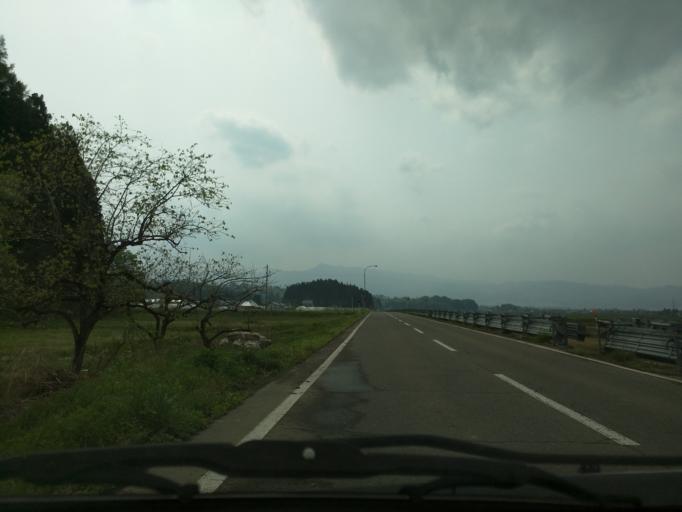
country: JP
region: Fukushima
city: Kitakata
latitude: 37.4360
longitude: 139.8778
